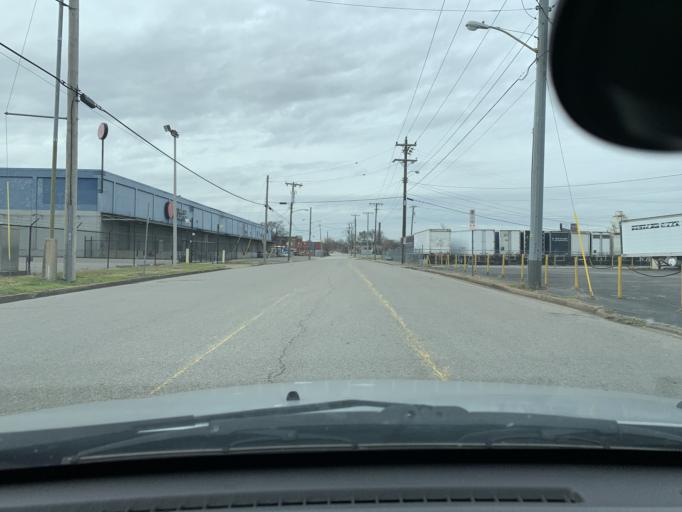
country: US
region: Tennessee
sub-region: Davidson County
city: Nashville
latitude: 36.1744
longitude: -86.7744
